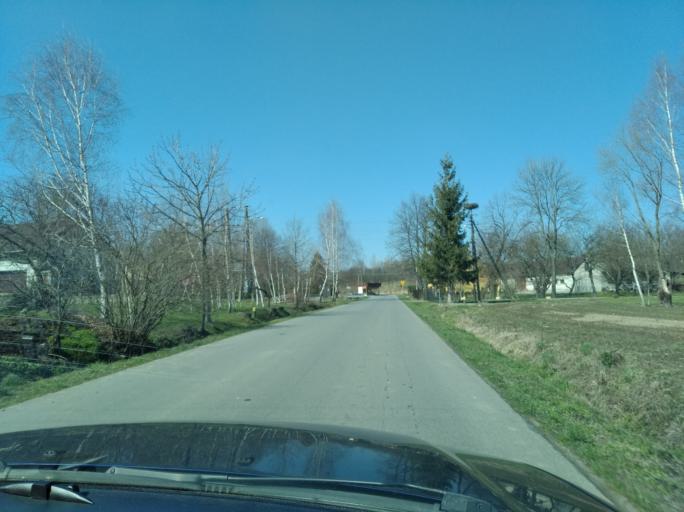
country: PL
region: Subcarpathian Voivodeship
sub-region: Powiat przeworski
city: Pantalowice
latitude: 49.9285
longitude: 22.4436
